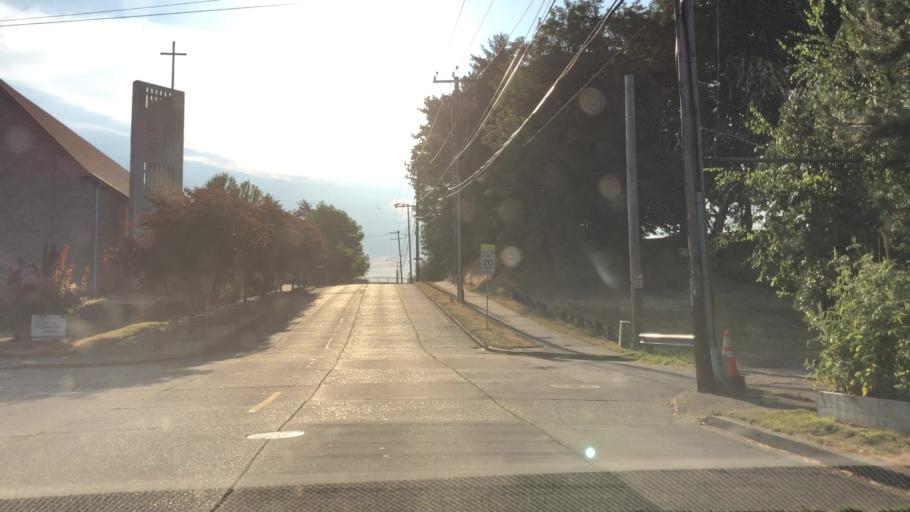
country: US
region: Washington
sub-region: King County
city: Yarrow Point
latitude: 47.6613
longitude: -122.2797
